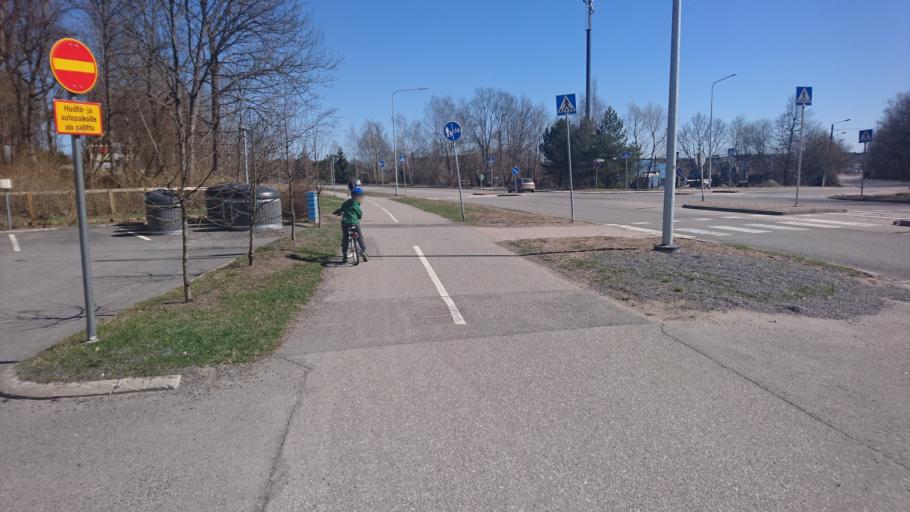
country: FI
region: Varsinais-Suomi
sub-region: Turku
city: Raisio
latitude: 60.4491
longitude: 22.1702
